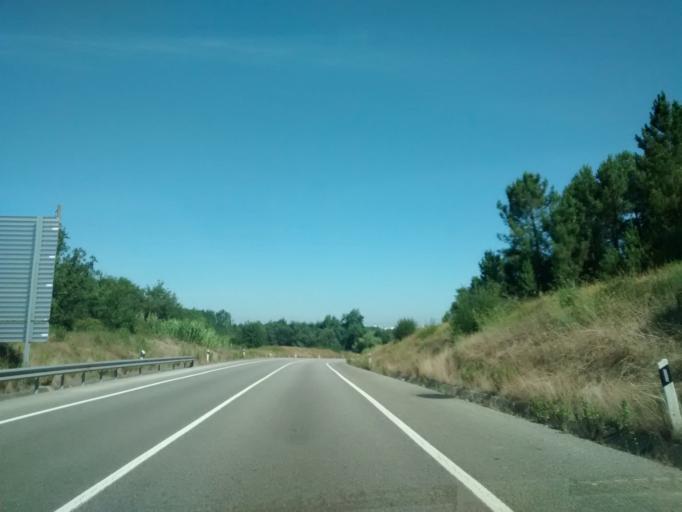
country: PT
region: Aveiro
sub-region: Anadia
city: Sangalhos
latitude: 40.4864
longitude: -8.4816
